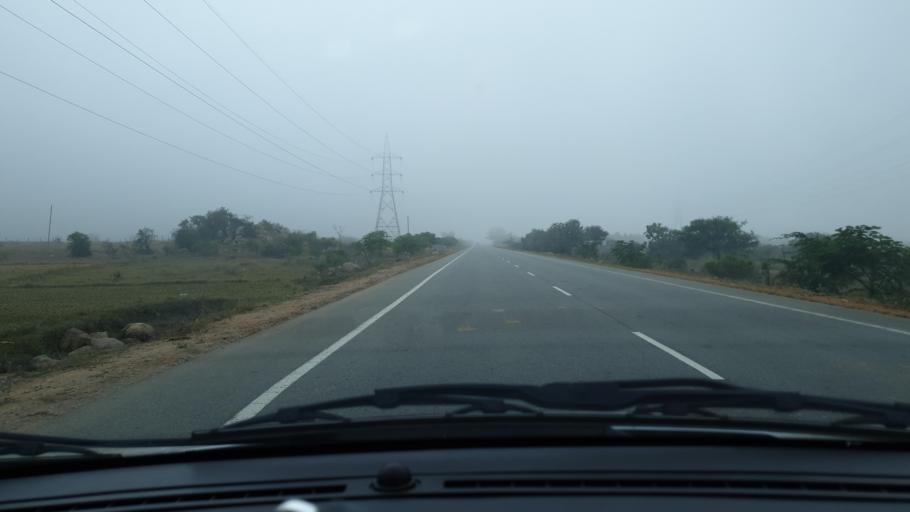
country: IN
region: Telangana
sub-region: Nalgonda
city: Devarkonda
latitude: 16.6262
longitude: 78.6664
